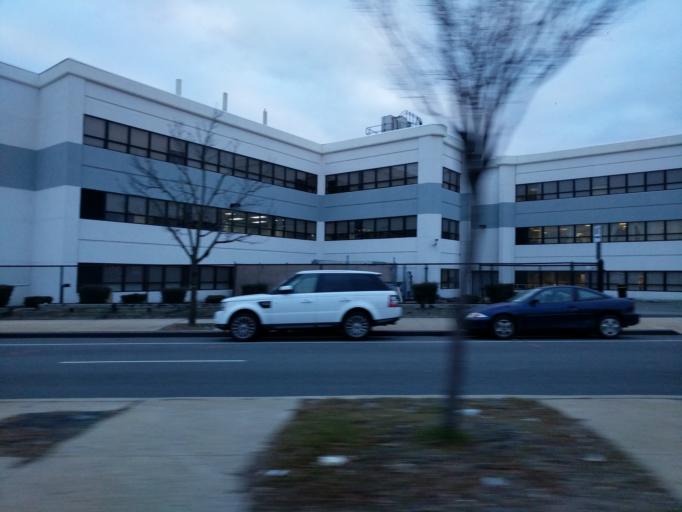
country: US
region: New York
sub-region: Nassau County
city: South Valley Stream
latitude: 40.6736
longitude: -73.7325
